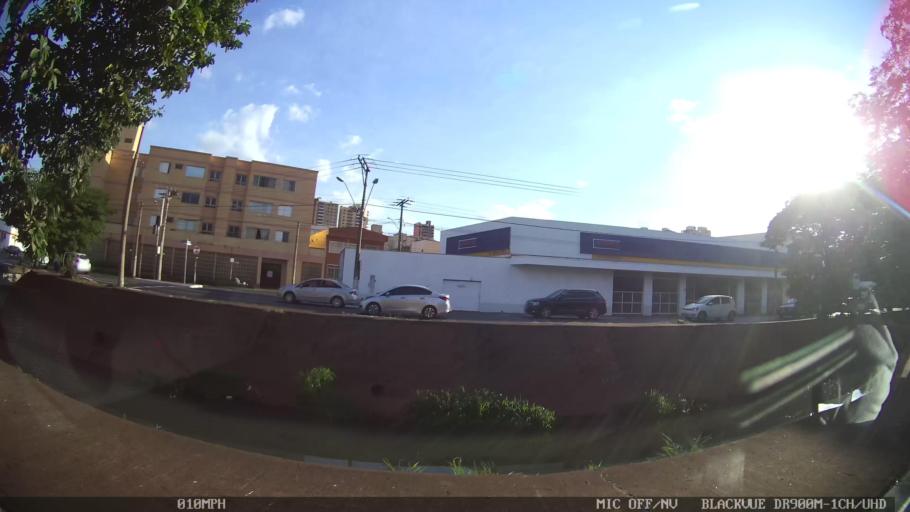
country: BR
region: Sao Paulo
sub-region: Ribeirao Preto
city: Ribeirao Preto
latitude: -21.1863
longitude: -47.7987
